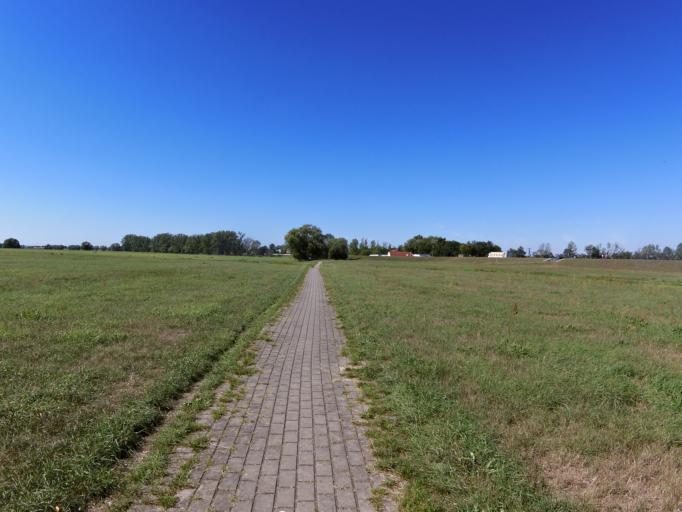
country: DE
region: Saxony-Anhalt
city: Elster
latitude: 51.8320
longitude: 12.7988
